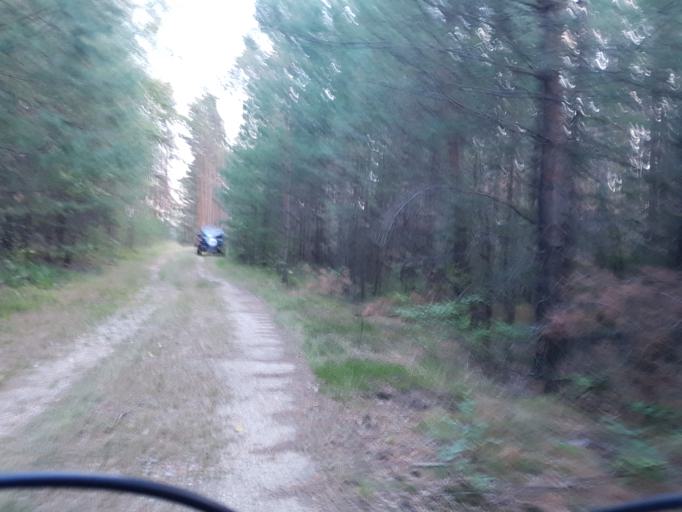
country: DE
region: Brandenburg
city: Trobitz
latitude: 51.5679
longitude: 13.4523
